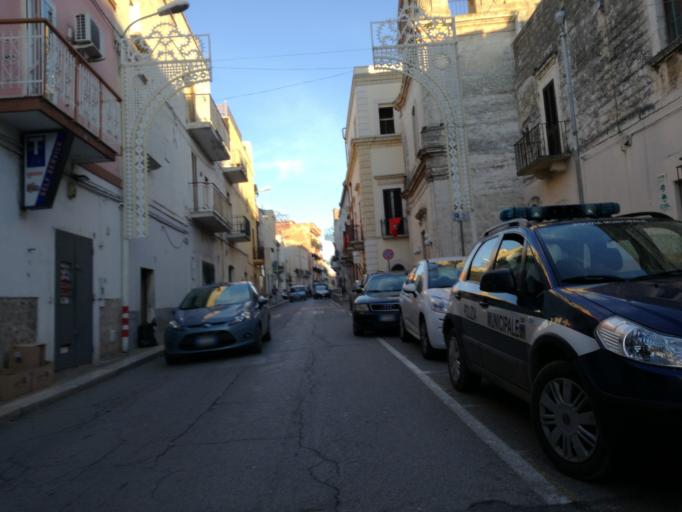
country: IT
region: Apulia
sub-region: Provincia di Bari
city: Adelfia
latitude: 41.0039
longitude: 16.8761
